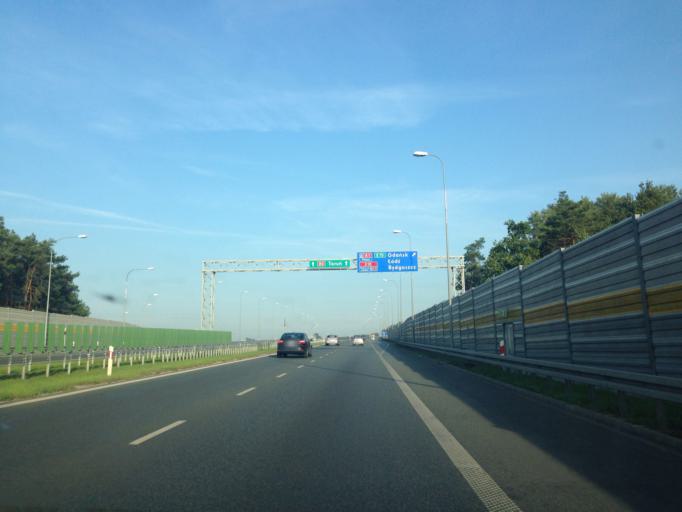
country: PL
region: Kujawsko-Pomorskie
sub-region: Powiat torunski
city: Lubicz Dolny
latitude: 53.0339
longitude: 18.7461
